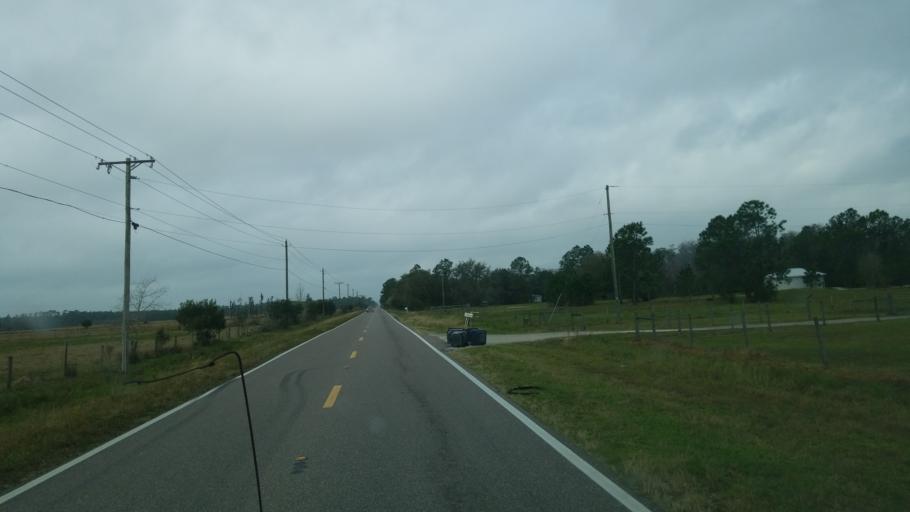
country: US
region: Florida
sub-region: Polk County
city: Polk City
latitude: 28.2592
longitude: -81.8612
